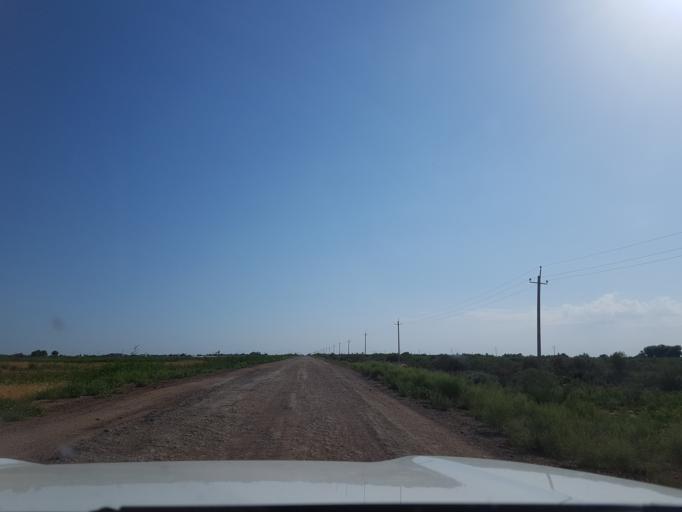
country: TM
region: Dasoguz
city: Koeneuergench
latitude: 42.0585
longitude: 58.8419
